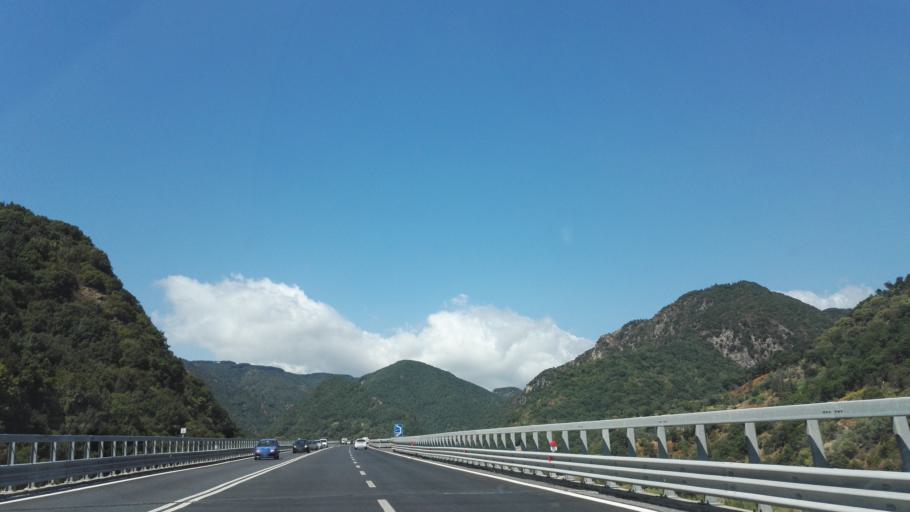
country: IT
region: Calabria
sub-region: Provincia di Reggio Calabria
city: Mammola
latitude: 38.3590
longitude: 16.2151
